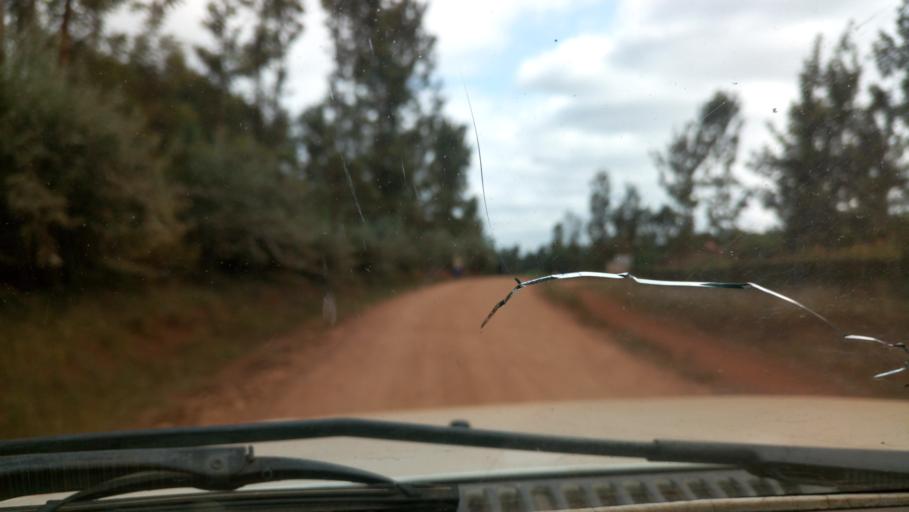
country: KE
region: Murang'a District
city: Maragua
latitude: -0.7576
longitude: 37.1051
